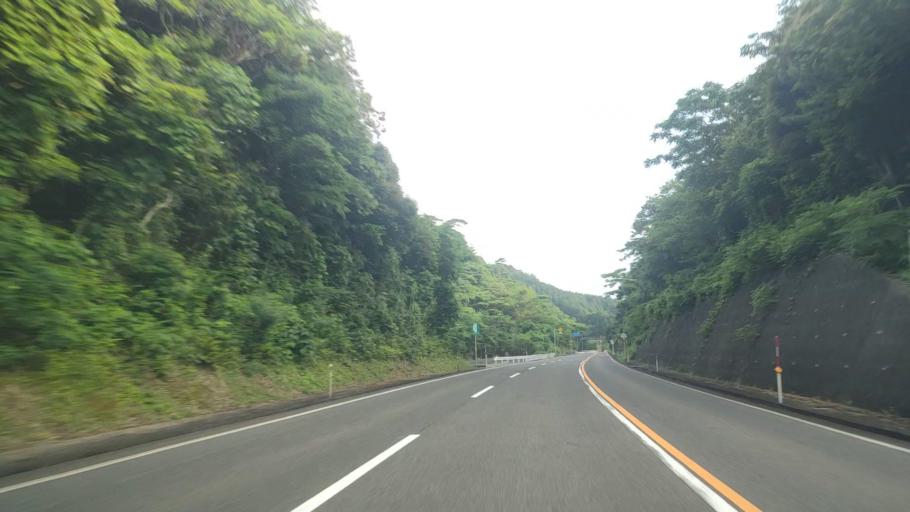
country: JP
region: Tottori
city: Kurayoshi
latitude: 35.3489
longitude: 133.7500
